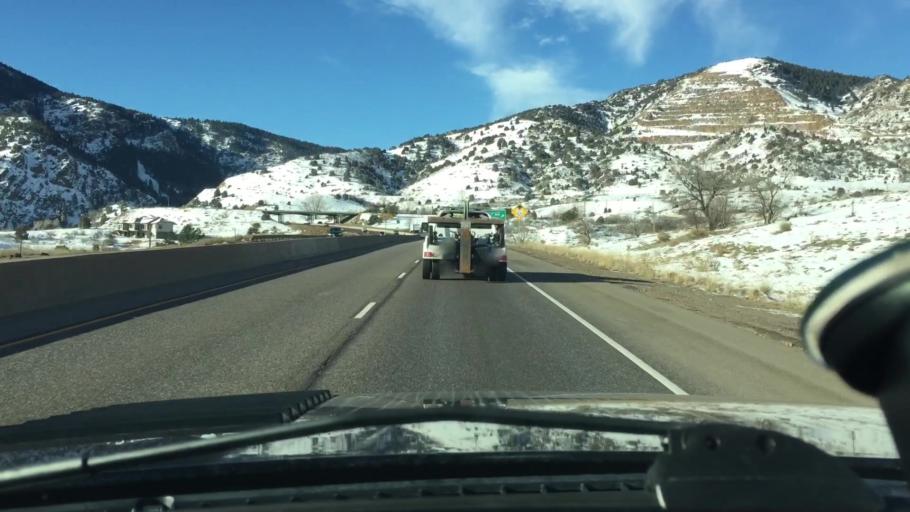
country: US
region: Colorado
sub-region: Jefferson County
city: Indian Hills
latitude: 39.6261
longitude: -105.1868
